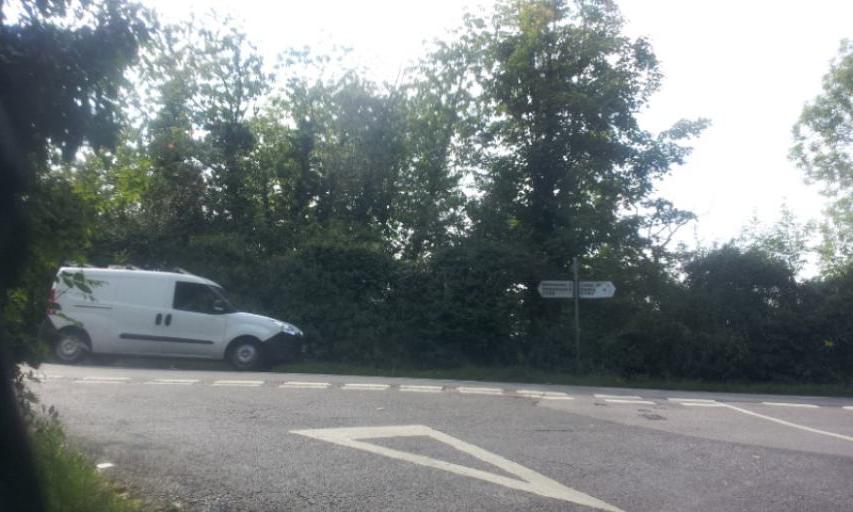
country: GB
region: England
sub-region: Kent
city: Marden
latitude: 51.1782
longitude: 0.4545
